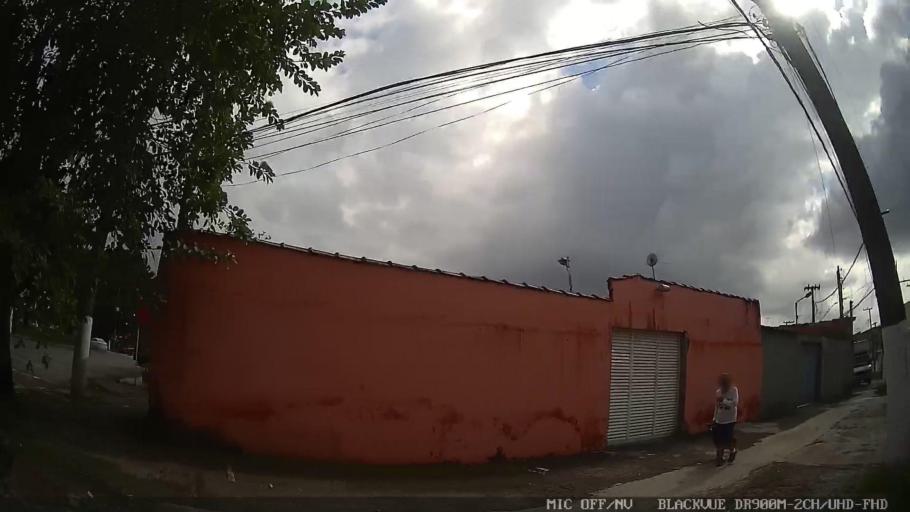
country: BR
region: Sao Paulo
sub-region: Guaruja
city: Guaruja
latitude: -23.9968
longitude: -46.2738
